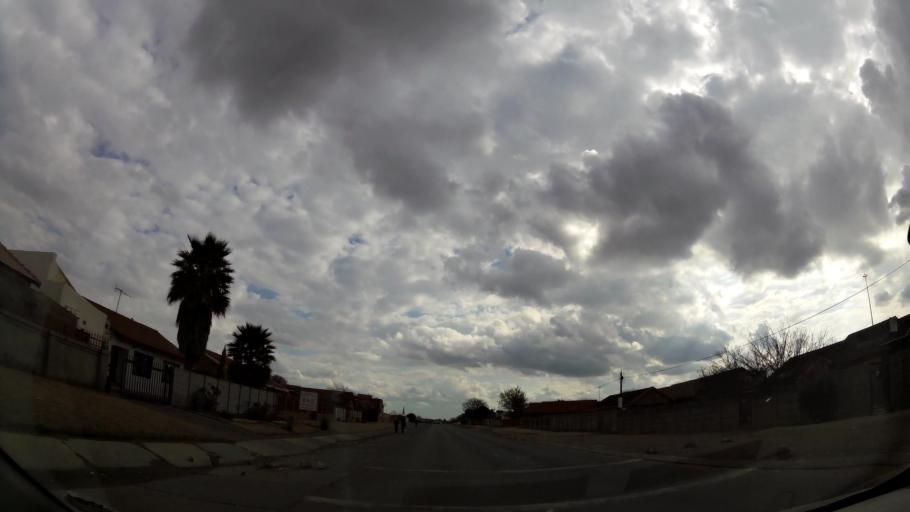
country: ZA
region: Orange Free State
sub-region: Fezile Dabi District Municipality
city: Sasolburg
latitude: -26.8495
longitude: 27.8573
